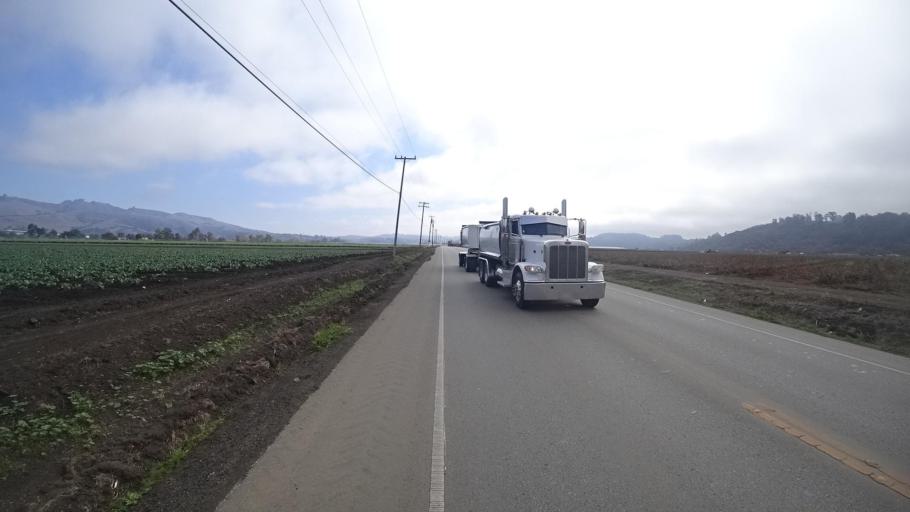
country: US
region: California
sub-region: Monterey County
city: Pajaro
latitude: 36.9026
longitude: -121.6998
